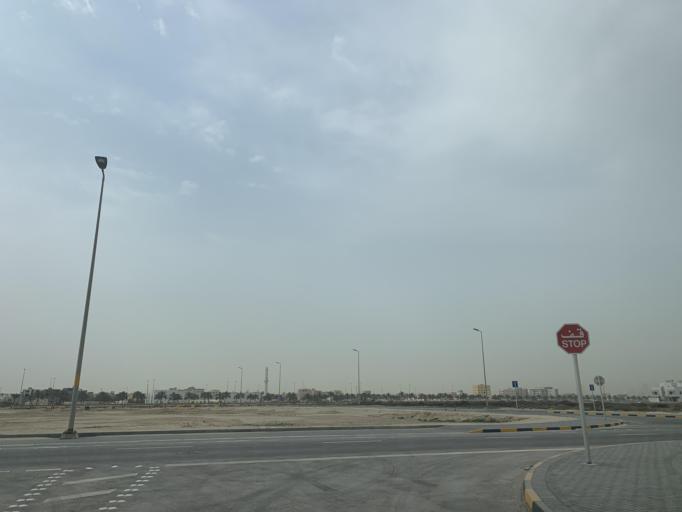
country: BH
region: Northern
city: Madinat `Isa
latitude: 26.1856
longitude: 50.5108
